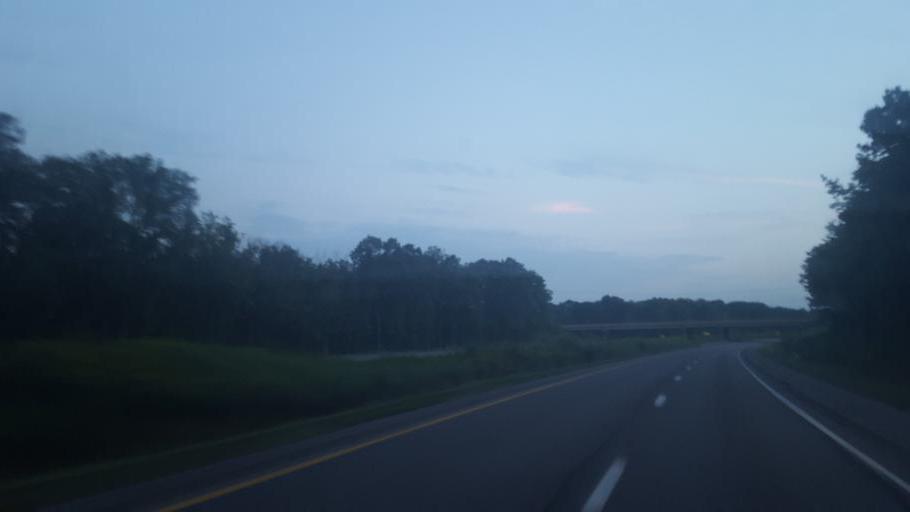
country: US
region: Pennsylvania
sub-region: Mercer County
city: Mercer
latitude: 41.2632
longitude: -80.1661
